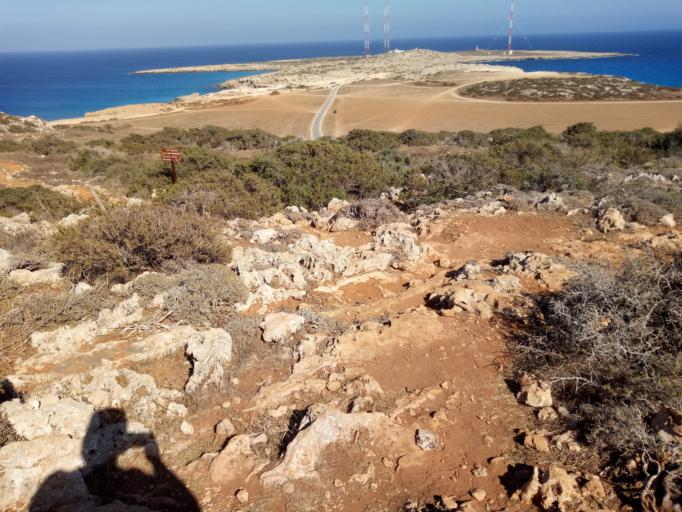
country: CY
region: Ammochostos
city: Protaras
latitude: 34.9687
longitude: 34.0718
